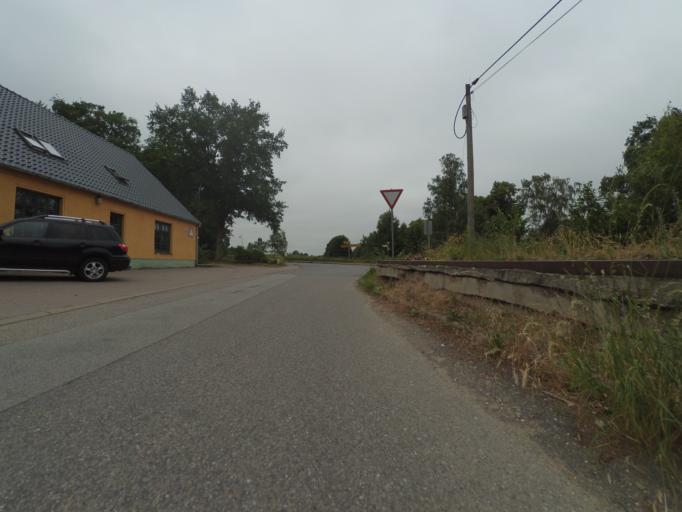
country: DE
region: Mecklenburg-Vorpommern
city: Dabel
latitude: 53.6612
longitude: 11.9422
